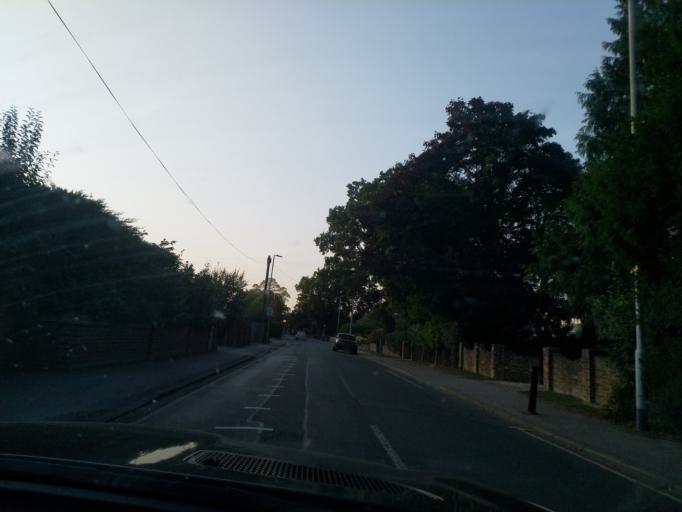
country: GB
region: England
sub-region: Kent
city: Sheerness
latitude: 51.4079
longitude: 0.8255
